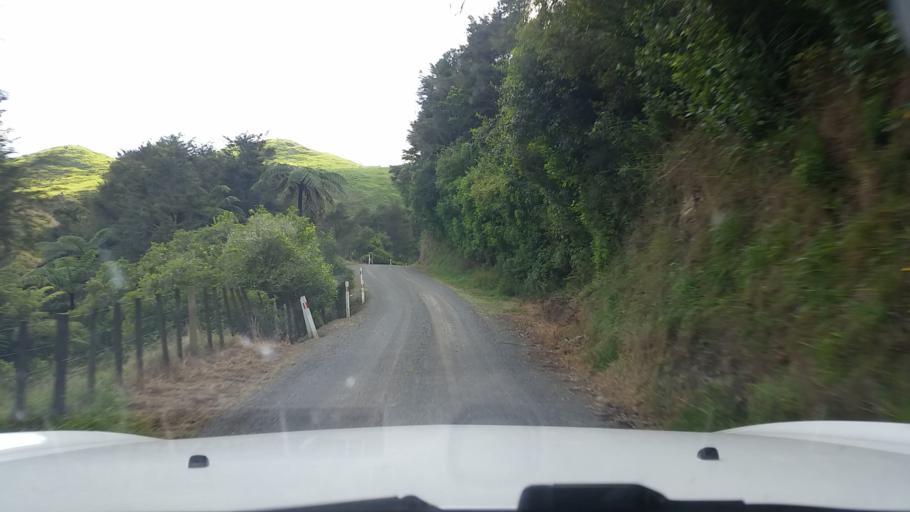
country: NZ
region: Waikato
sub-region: Hauraki District
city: Ngatea
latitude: -37.4725
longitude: 175.4568
